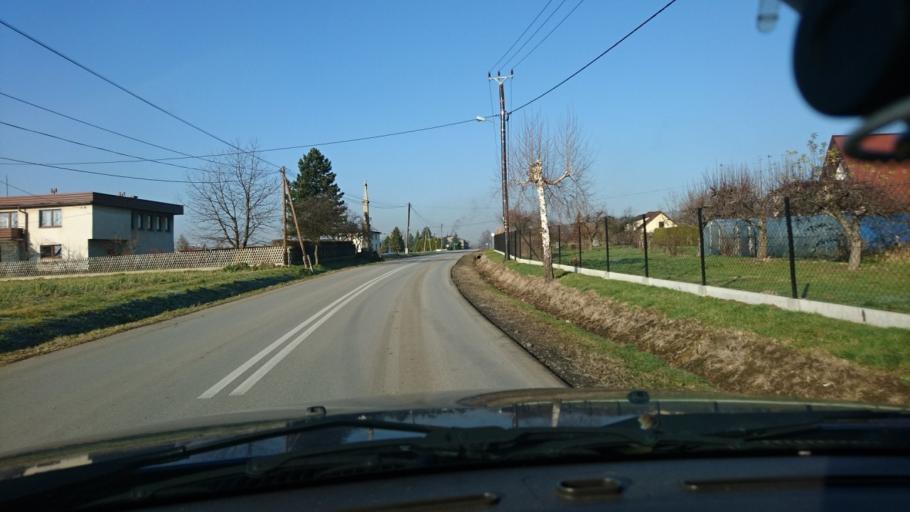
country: PL
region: Silesian Voivodeship
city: Janowice
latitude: 49.8826
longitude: 19.0992
